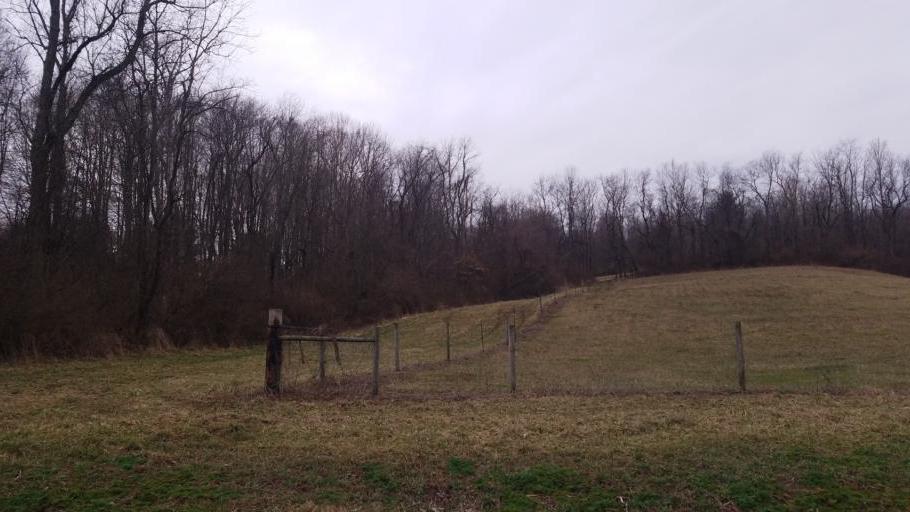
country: US
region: Ohio
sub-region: Richland County
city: Mansfield
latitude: 40.7273
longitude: -82.4894
